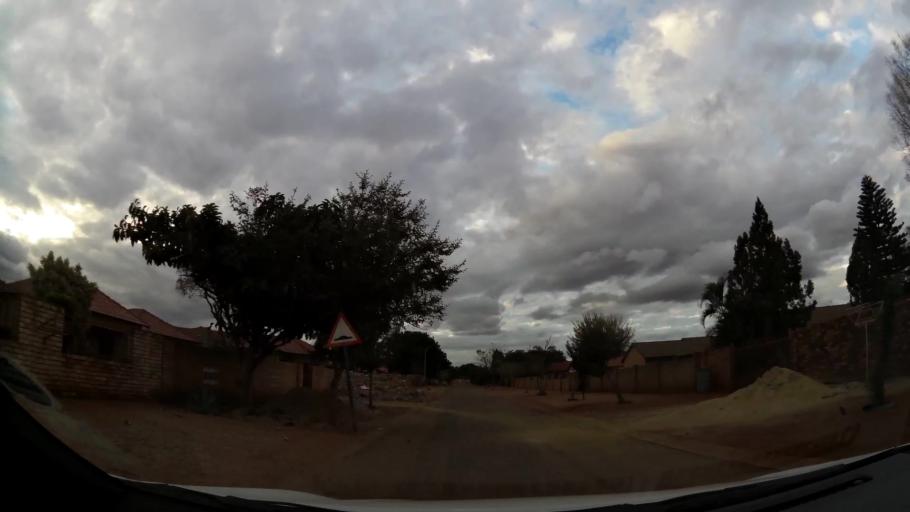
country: ZA
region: Limpopo
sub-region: Waterberg District Municipality
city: Mokopane
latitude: -24.1988
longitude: 28.9929
